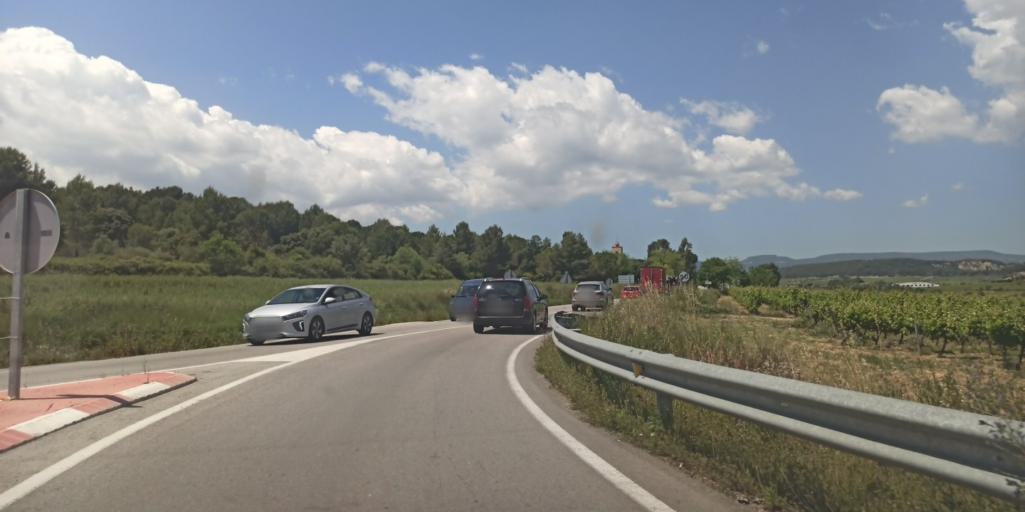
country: ES
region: Catalonia
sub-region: Provincia de Barcelona
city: Vilobi del Penedes
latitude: 41.3586
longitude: 1.6636
